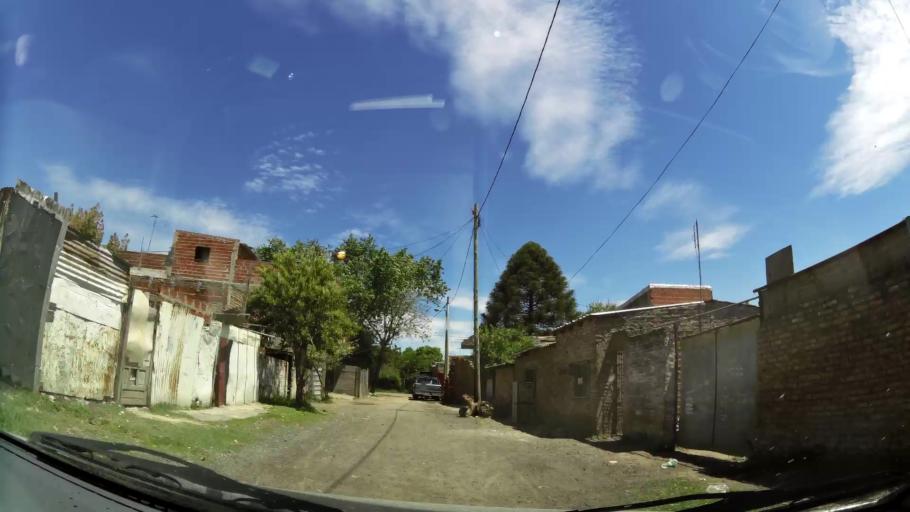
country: AR
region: Buenos Aires
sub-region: Partido de Lanus
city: Lanus
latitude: -34.7255
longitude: -58.3305
